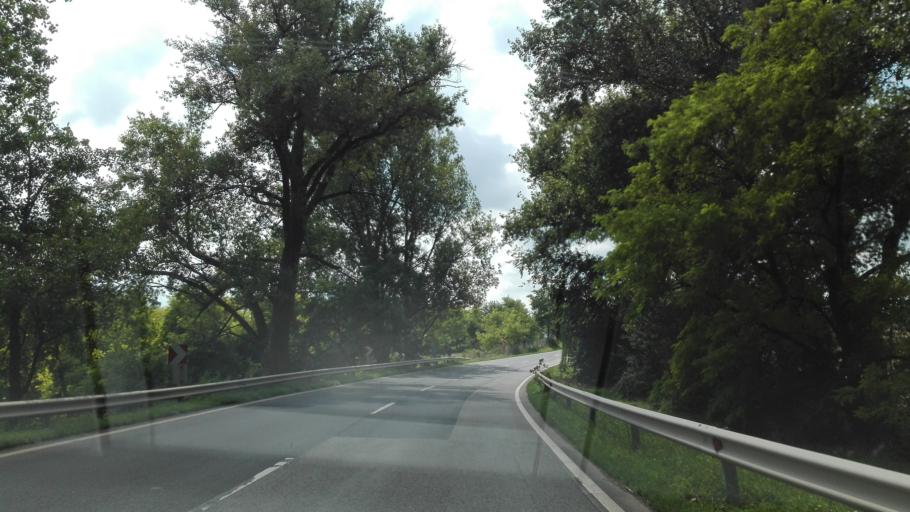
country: HU
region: Fejer
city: Eloszallas
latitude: 46.8155
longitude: 18.7882
